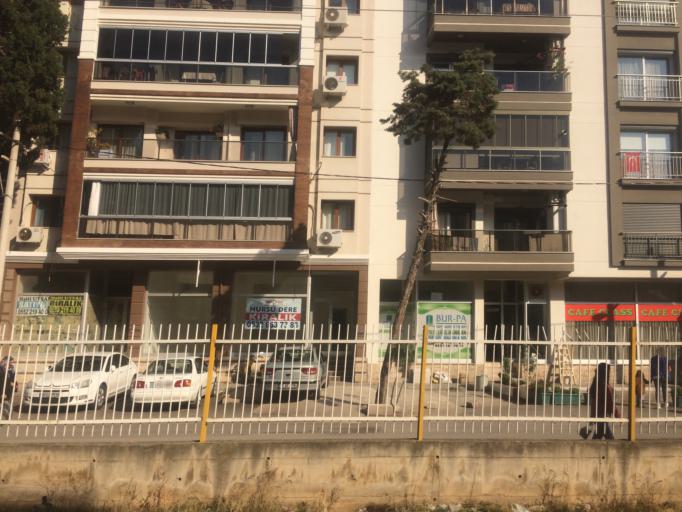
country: TR
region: Izmir
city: Karsiyaka
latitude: 38.4719
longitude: 27.0929
